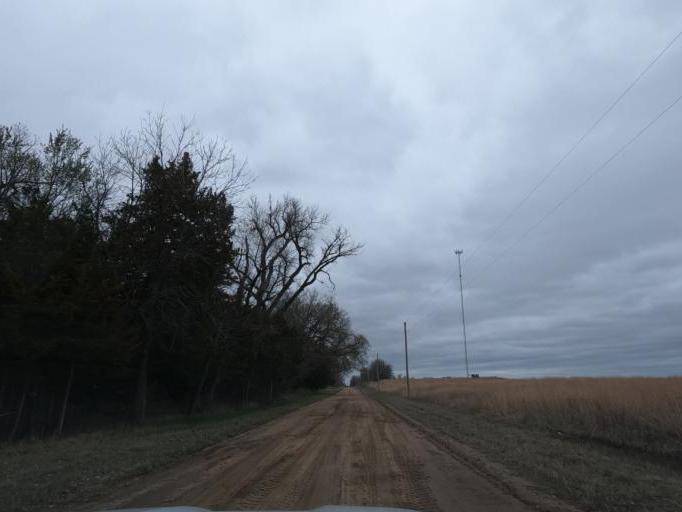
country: US
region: Kansas
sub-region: Rice County
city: Sterling
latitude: 37.9828
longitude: -98.3073
